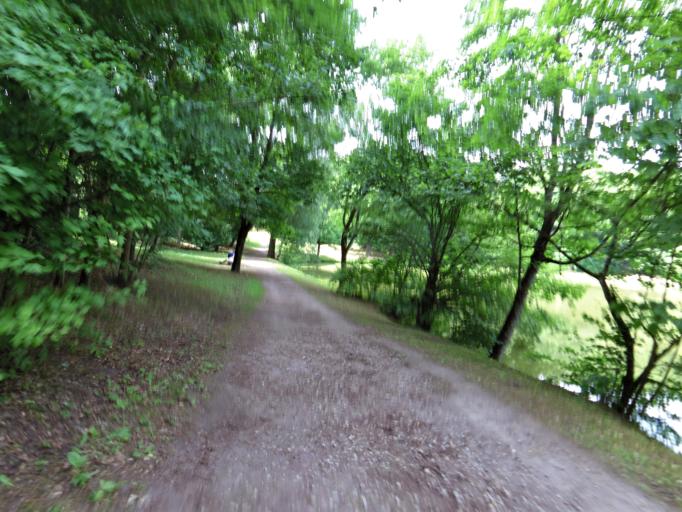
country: LT
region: Vilnius County
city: Rasos
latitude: 54.6722
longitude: 25.3259
